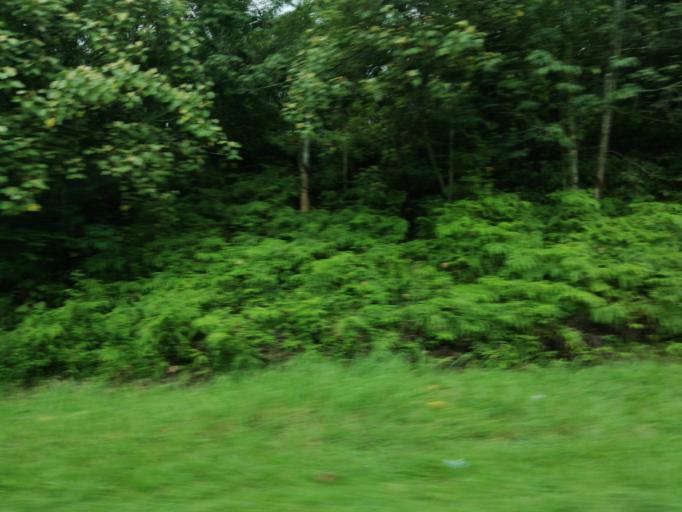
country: MY
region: Penang
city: Tasek Glugor
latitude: 5.4950
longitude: 100.6082
